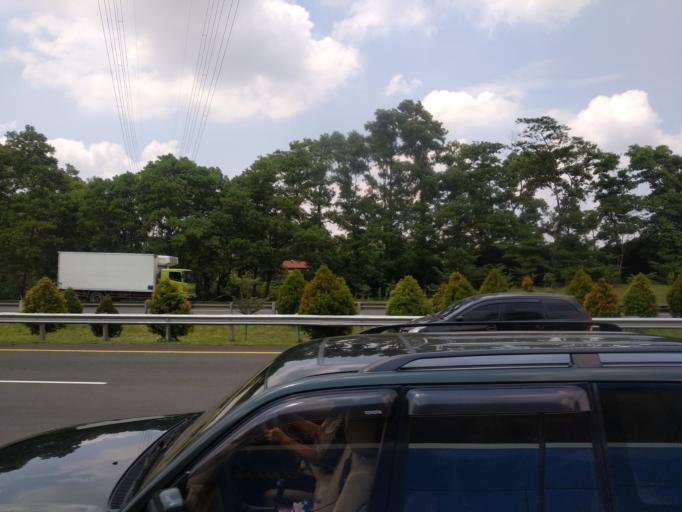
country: ID
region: West Java
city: Bogor
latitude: -6.5915
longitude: 106.8344
